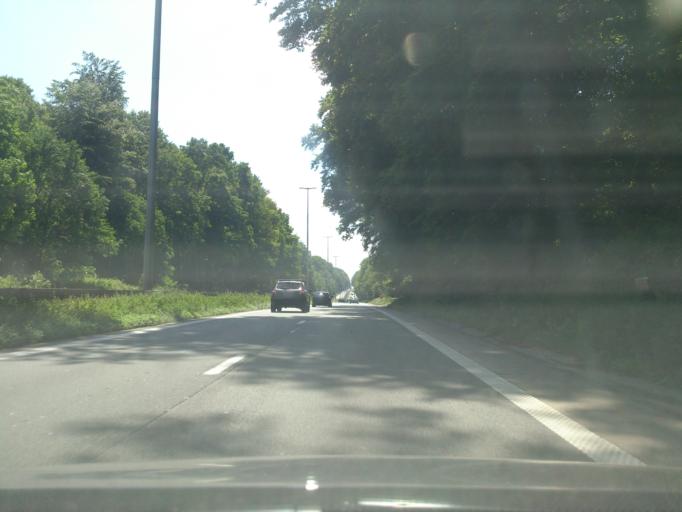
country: BE
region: Flanders
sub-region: Provincie Vlaams-Brabant
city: Hoeilaart
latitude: 50.7635
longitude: 4.4404
